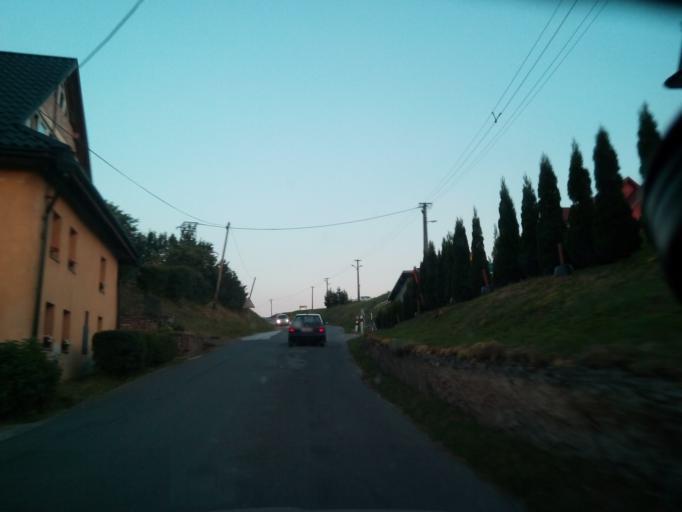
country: SK
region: Presovsky
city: Lubica
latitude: 49.0851
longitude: 20.4260
